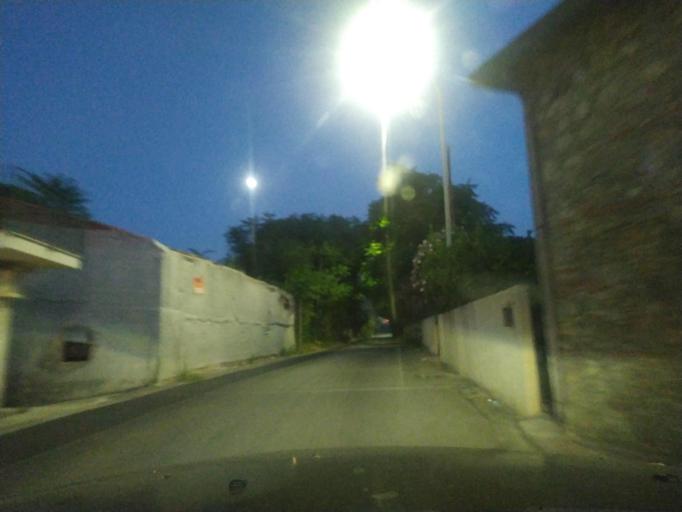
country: IT
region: Sicily
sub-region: Messina
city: Terme
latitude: 38.1453
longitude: 15.1588
